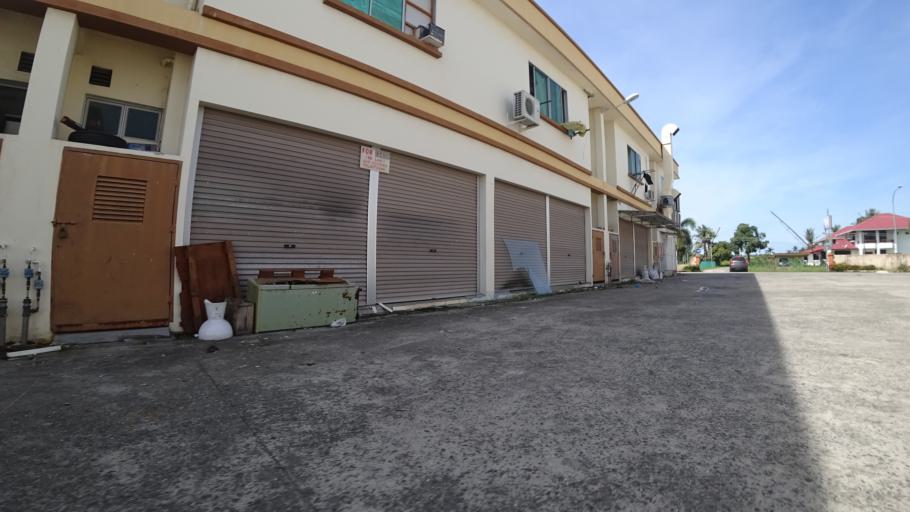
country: BN
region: Brunei and Muara
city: Bandar Seri Begawan
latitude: 4.8724
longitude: 114.8494
